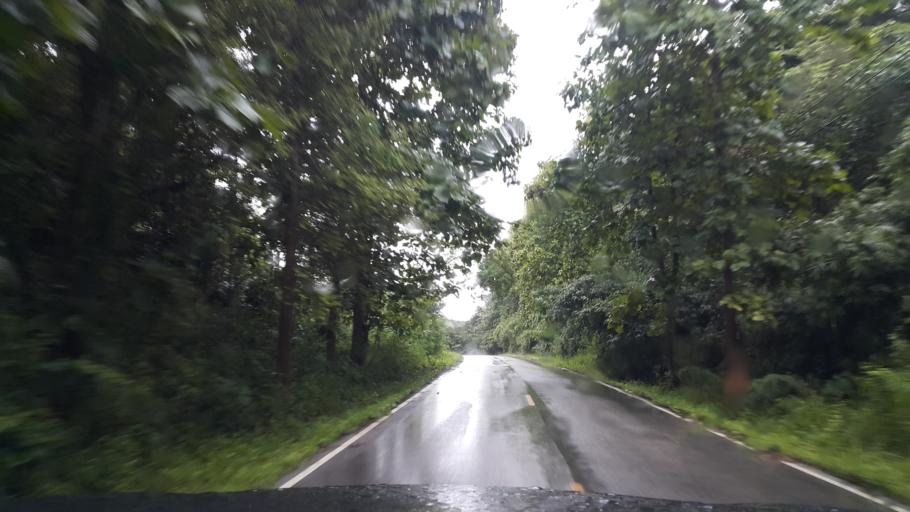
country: TH
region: Phayao
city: Phu Sang
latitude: 19.6090
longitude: 100.4077
